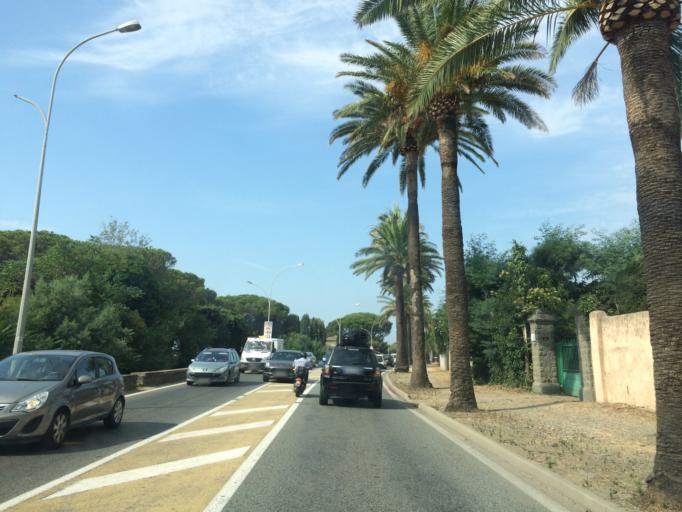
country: FR
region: Provence-Alpes-Cote d'Azur
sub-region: Departement du Var
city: Sainte-Maxime
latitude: 43.2888
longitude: 6.6042
